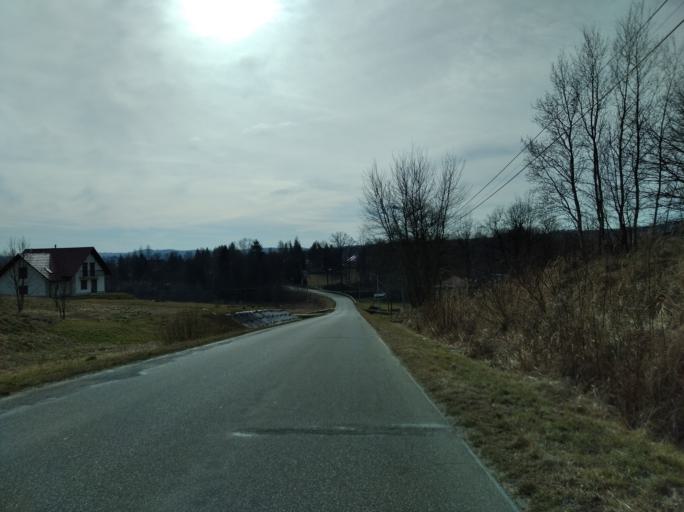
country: PL
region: Subcarpathian Voivodeship
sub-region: Powiat brzozowski
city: Orzechowka
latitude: 49.7407
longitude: 21.9419
